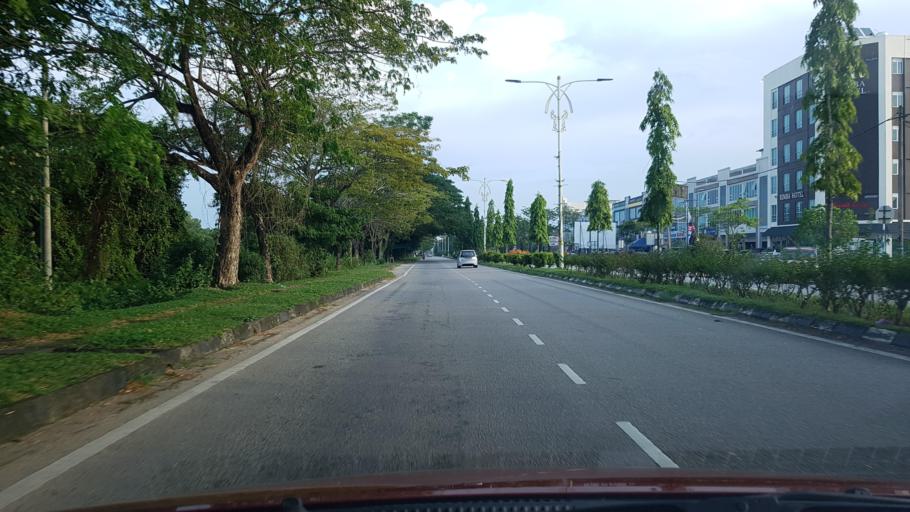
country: MY
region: Terengganu
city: Kuala Terengganu
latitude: 5.3498
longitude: 103.1030
